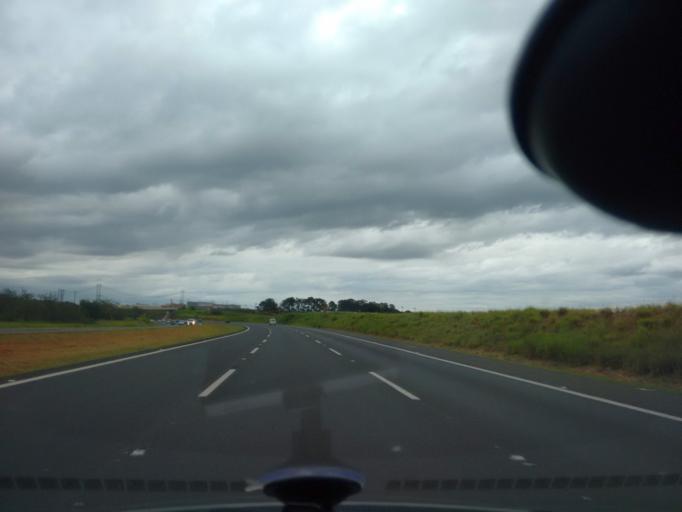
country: BR
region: Sao Paulo
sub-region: Hortolandia
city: Hortolandia
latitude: -22.8884
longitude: -47.2289
